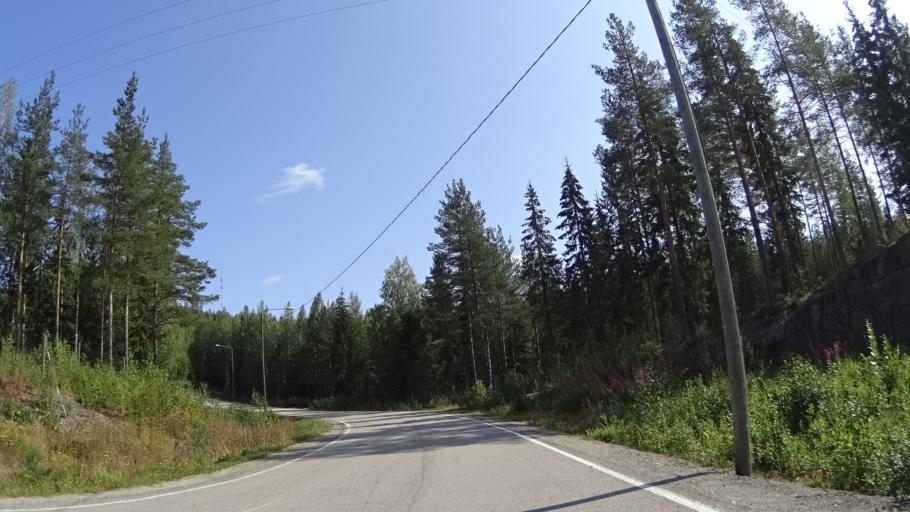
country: FI
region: Central Finland
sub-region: Jaemsae
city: Jaemsae
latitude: 61.7752
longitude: 24.8899
